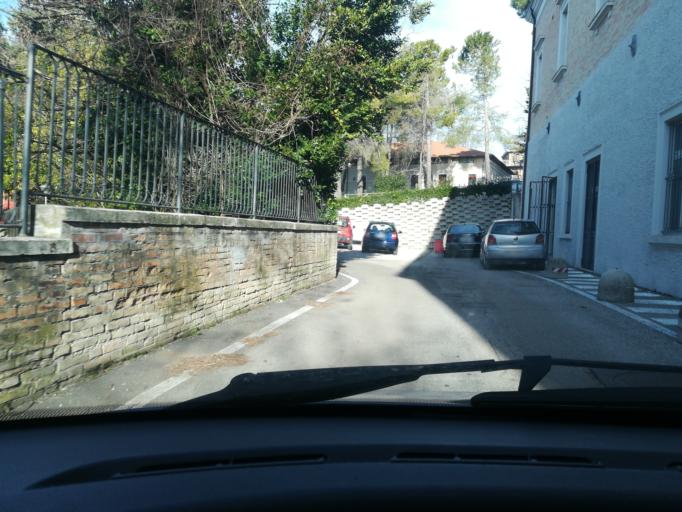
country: IT
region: The Marches
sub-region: Provincia di Macerata
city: Macerata
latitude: 43.2976
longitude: 13.4339
